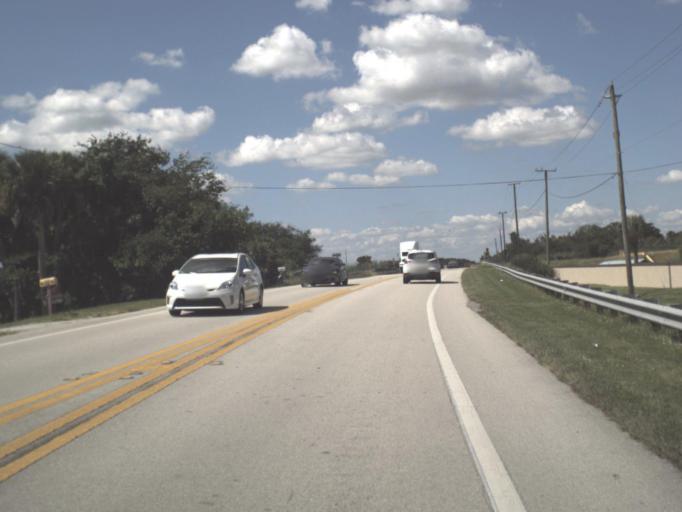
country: US
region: Florida
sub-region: Okeechobee County
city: Taylor Creek
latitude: 27.1926
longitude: -80.7592
